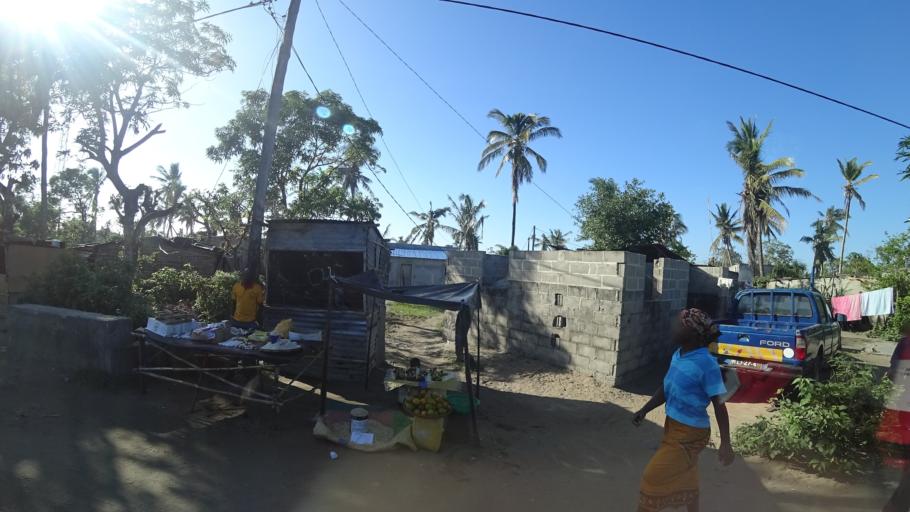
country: MZ
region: Sofala
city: Beira
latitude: -19.7741
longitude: 34.8848
